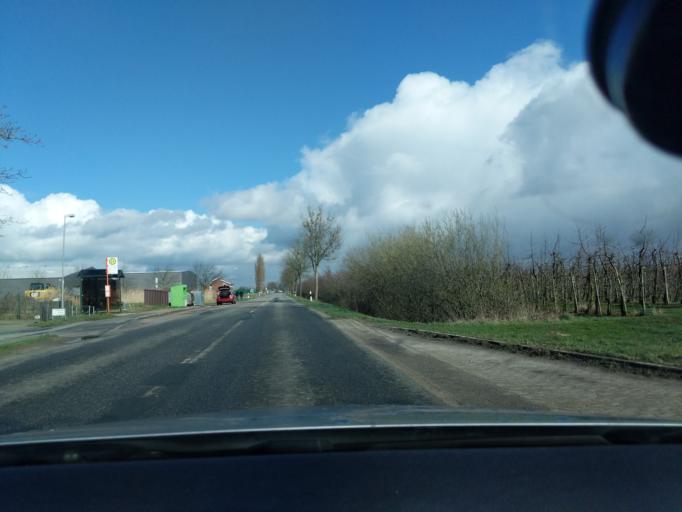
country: DE
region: Lower Saxony
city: Stade
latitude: 53.6041
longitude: 9.5175
